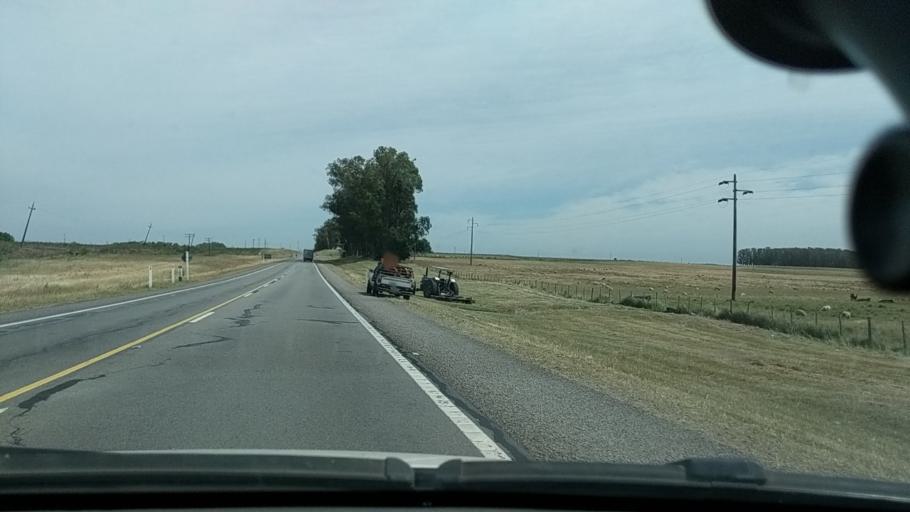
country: UY
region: Durazno
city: Durazno
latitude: -33.5225
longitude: -56.4053
